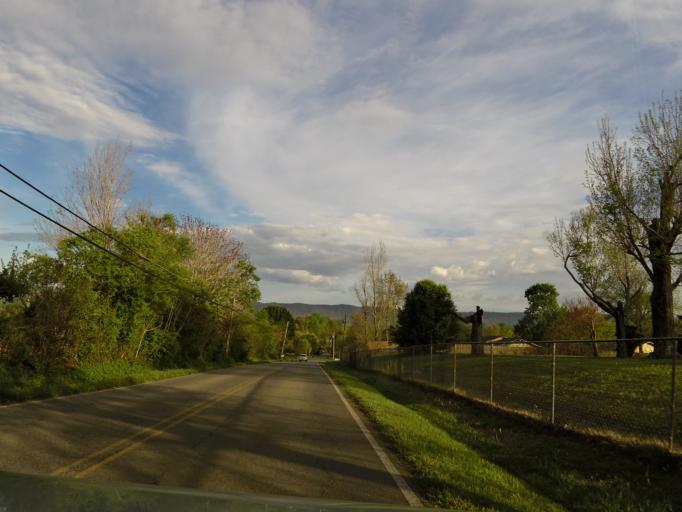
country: US
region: Tennessee
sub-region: Blount County
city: Maryville
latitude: 35.6848
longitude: -84.0156
